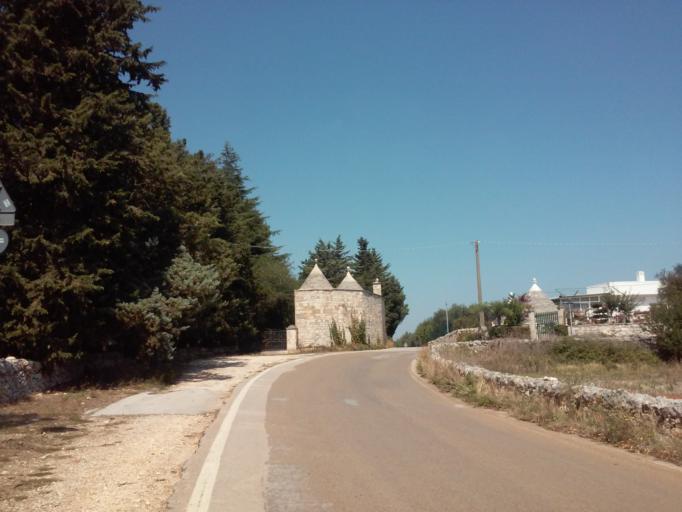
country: IT
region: Apulia
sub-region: Provincia di Bari
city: Alberobello
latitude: 40.7937
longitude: 17.2212
